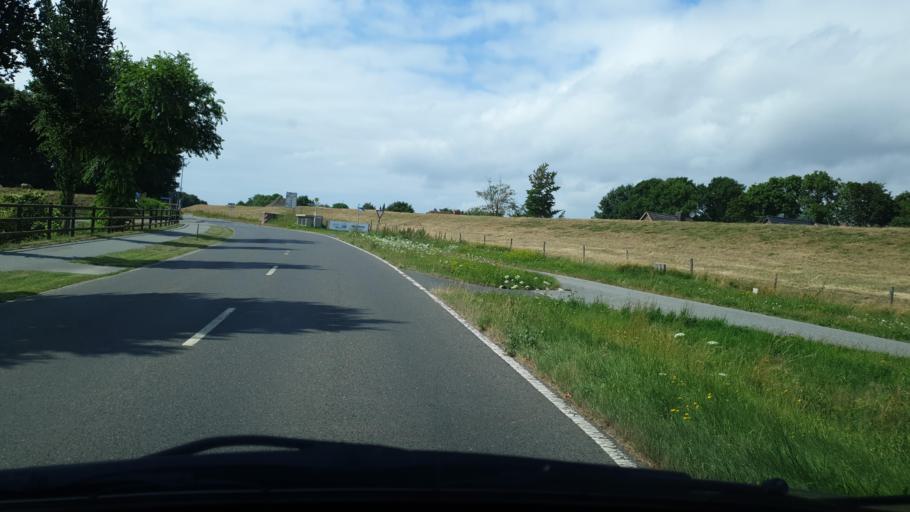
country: DE
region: Schleswig-Holstein
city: Friedrichskoog
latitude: 54.0045
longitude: 8.8859
